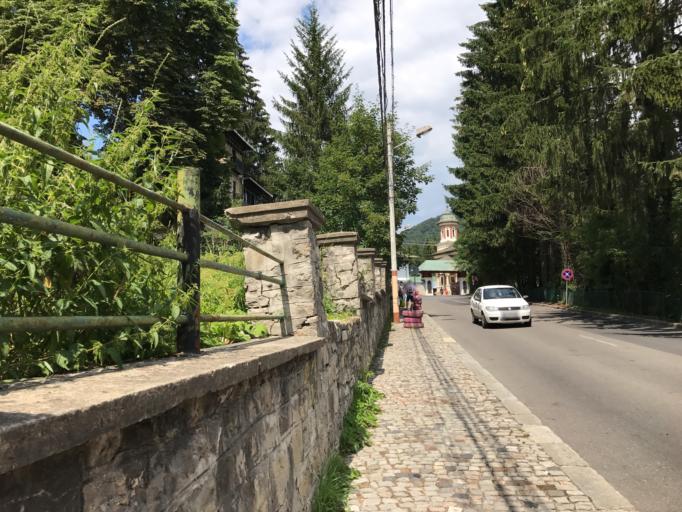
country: RO
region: Prahova
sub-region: Oras Sinaia
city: Sinaia
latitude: 45.3544
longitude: 25.5485
